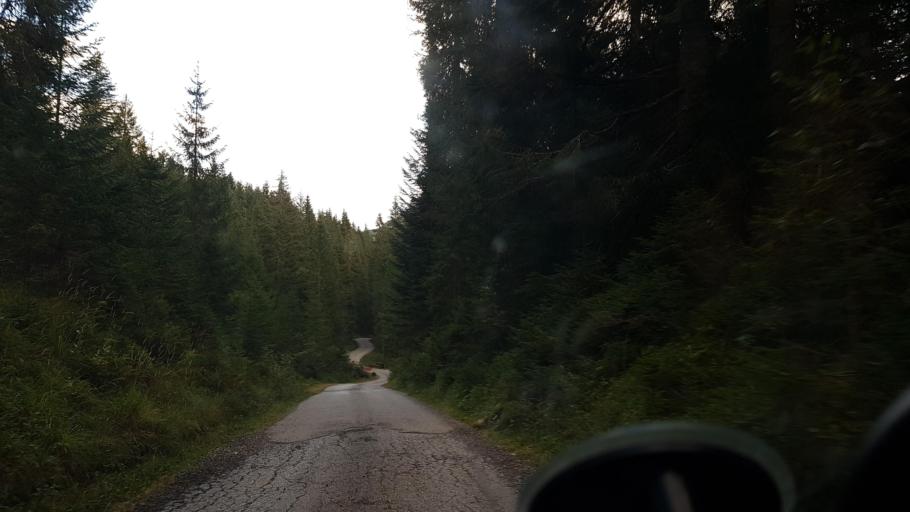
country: IT
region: Veneto
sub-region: Provincia di Belluno
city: San Pietro di Cadore
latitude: 46.6085
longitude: 12.6006
